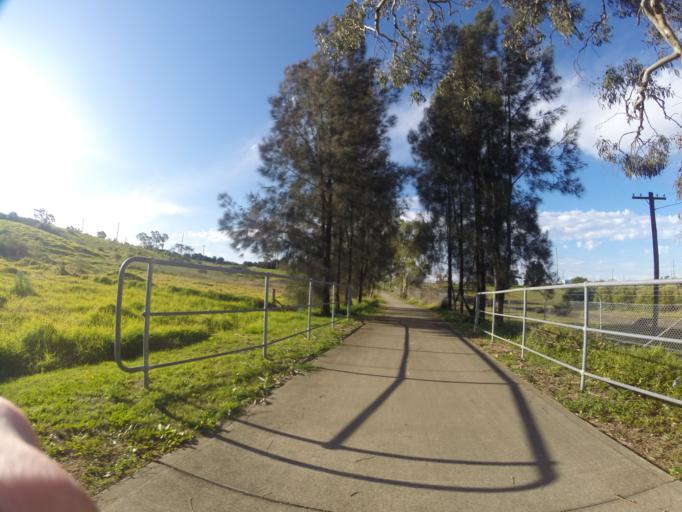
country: AU
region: New South Wales
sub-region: Fairfield
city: Horsley Park
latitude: -33.8472
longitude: 150.8714
